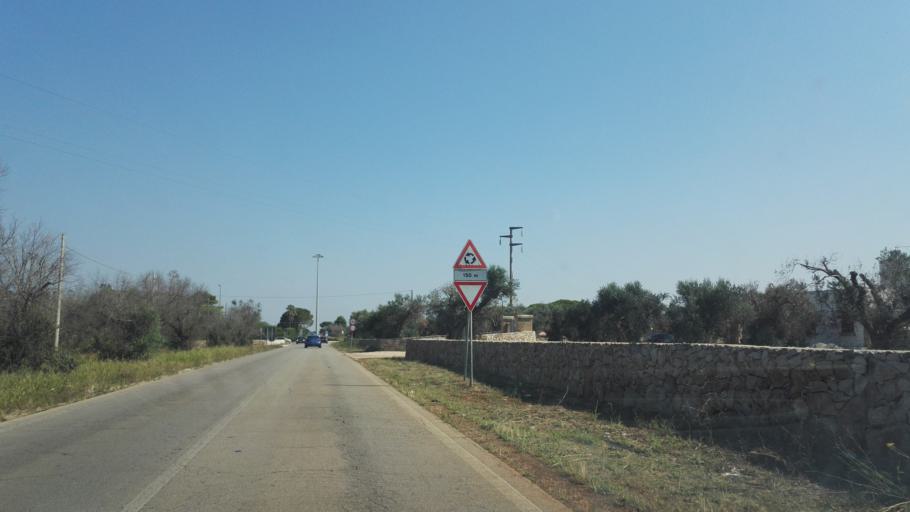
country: IT
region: Apulia
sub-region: Provincia di Lecce
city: Nardo
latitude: 40.1260
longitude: 18.0196
